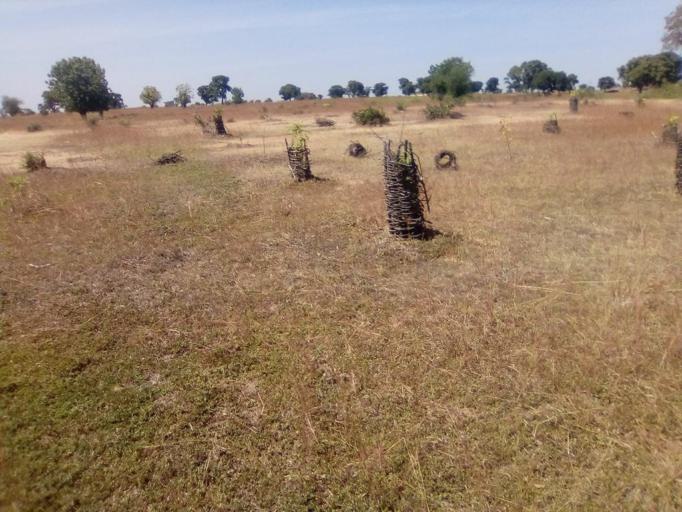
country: GH
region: Upper East
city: Bawku
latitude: 11.0944
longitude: -0.0721
